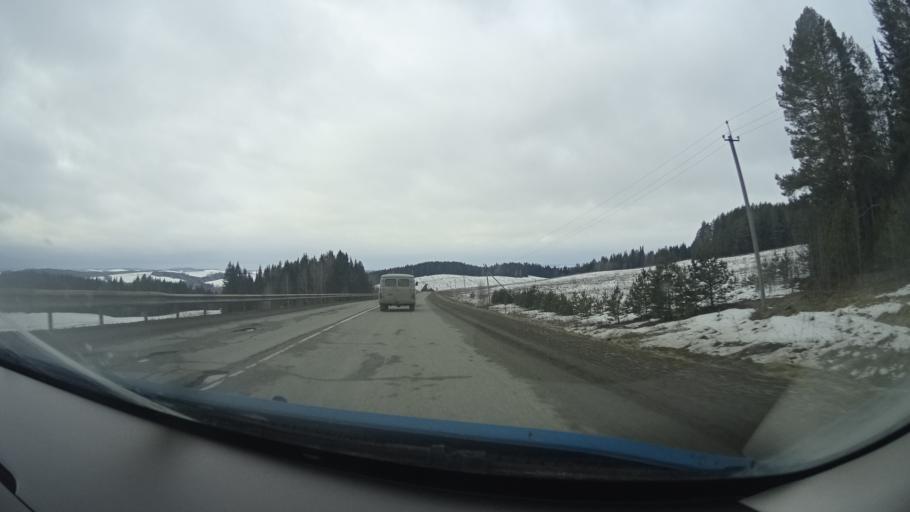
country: RU
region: Perm
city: Osa
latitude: 57.3146
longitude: 55.6232
